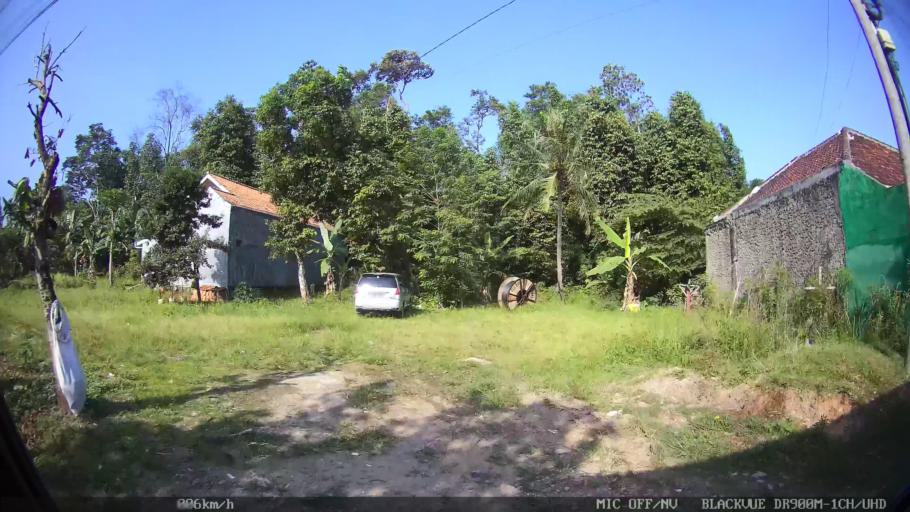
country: ID
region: Lampung
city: Kedaton
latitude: -5.3778
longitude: 105.2318
